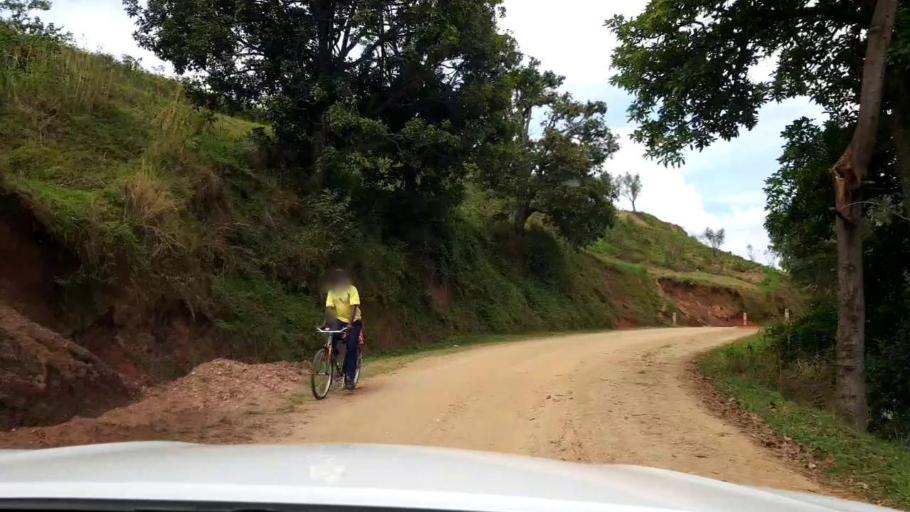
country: RW
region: Southern Province
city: Gitarama
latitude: -1.9855
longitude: 29.7074
